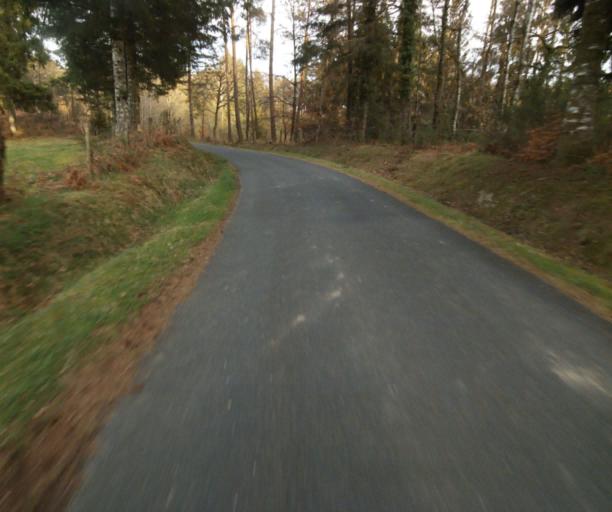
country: FR
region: Limousin
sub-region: Departement de la Correze
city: Argentat
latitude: 45.2422
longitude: 1.9616
